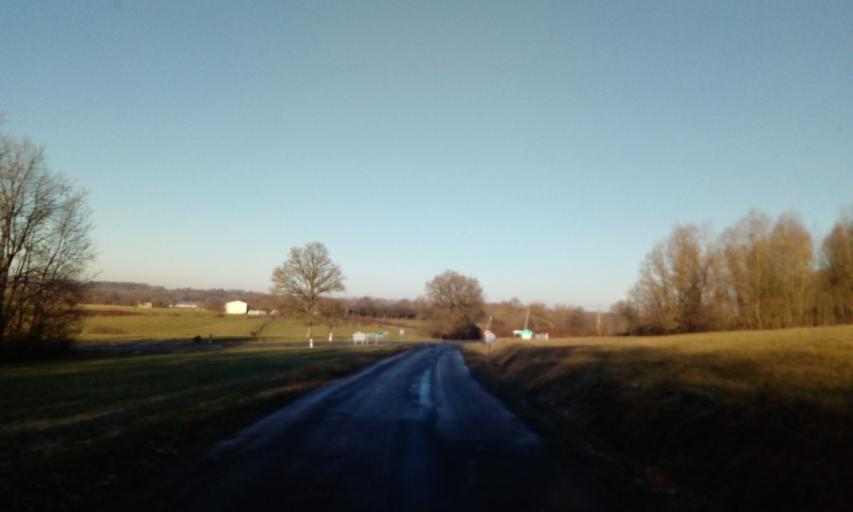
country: FR
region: Champagne-Ardenne
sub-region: Departement des Ardennes
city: Signy-le-Petit
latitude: 49.7385
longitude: 4.2937
